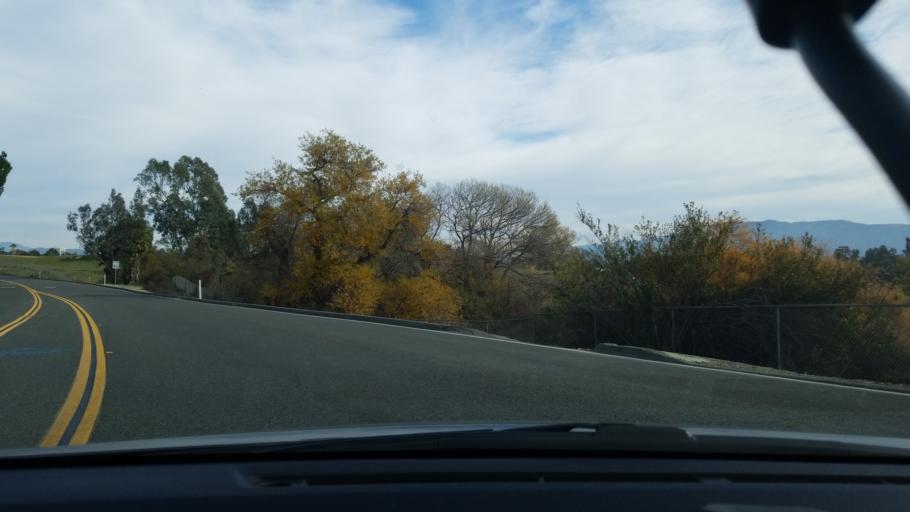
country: US
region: California
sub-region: Riverside County
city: Temecula
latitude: 33.5040
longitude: -117.1131
